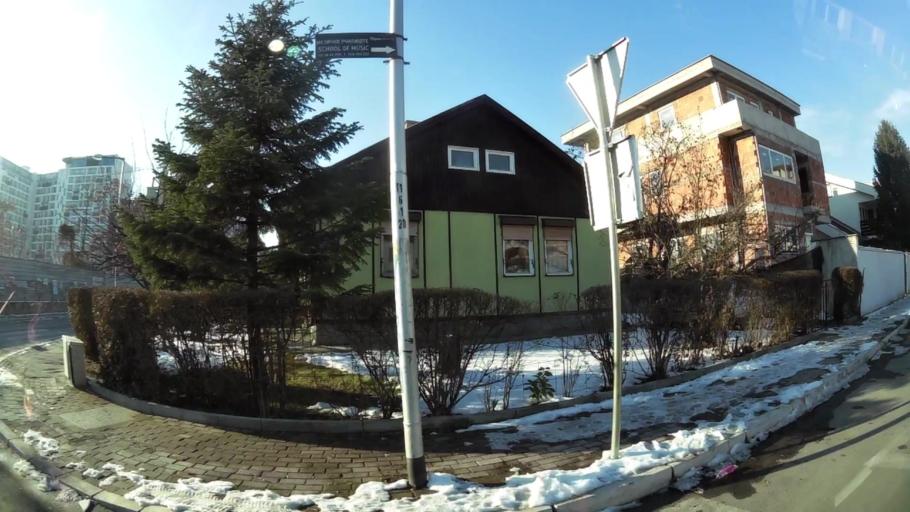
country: MK
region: Karpos
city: Skopje
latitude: 41.9984
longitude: 21.4003
